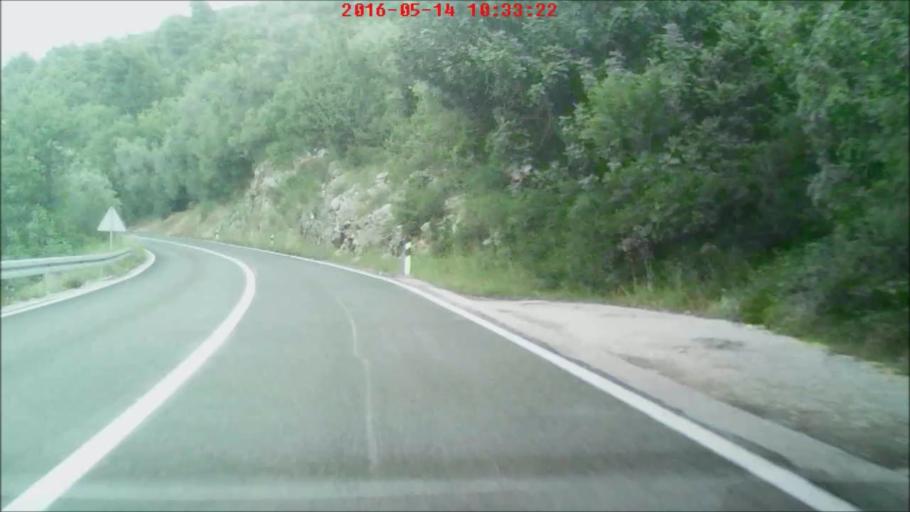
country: HR
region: Dubrovacko-Neretvanska
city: Podgora
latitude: 42.7729
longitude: 17.8868
